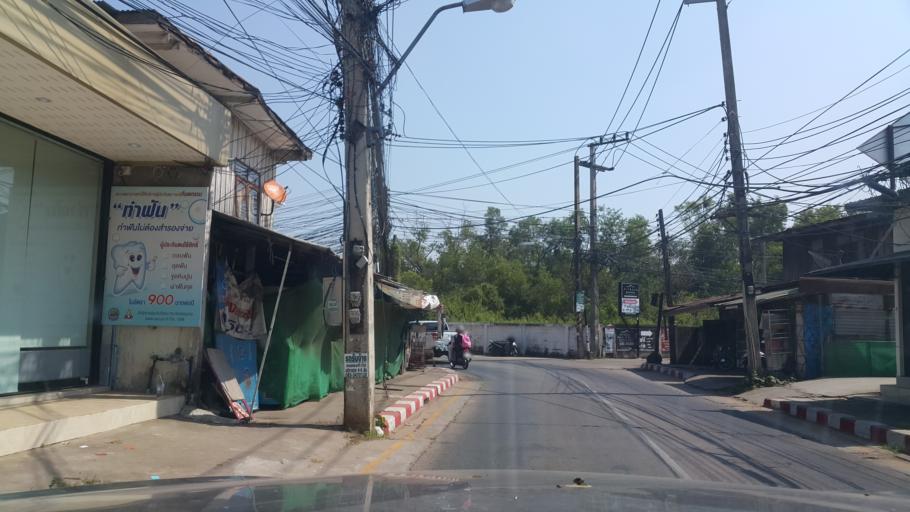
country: TH
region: Changwat Udon Thani
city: Udon Thani
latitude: 17.3938
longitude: 102.7946
